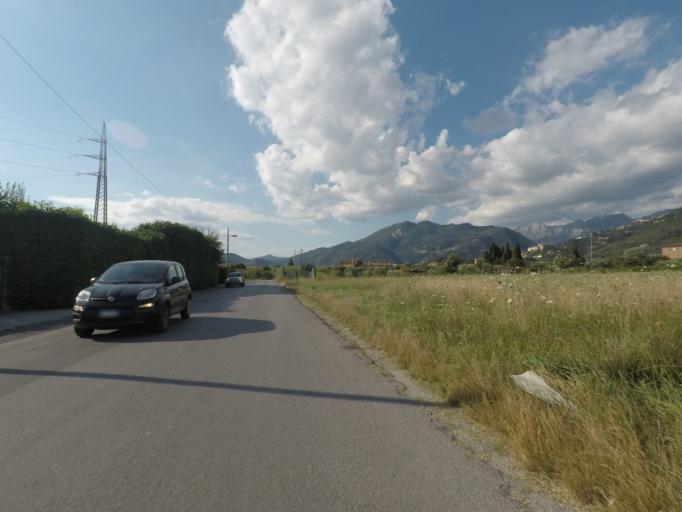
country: IT
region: Tuscany
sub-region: Provincia di Massa-Carrara
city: Massa
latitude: 44.0172
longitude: 10.1382
